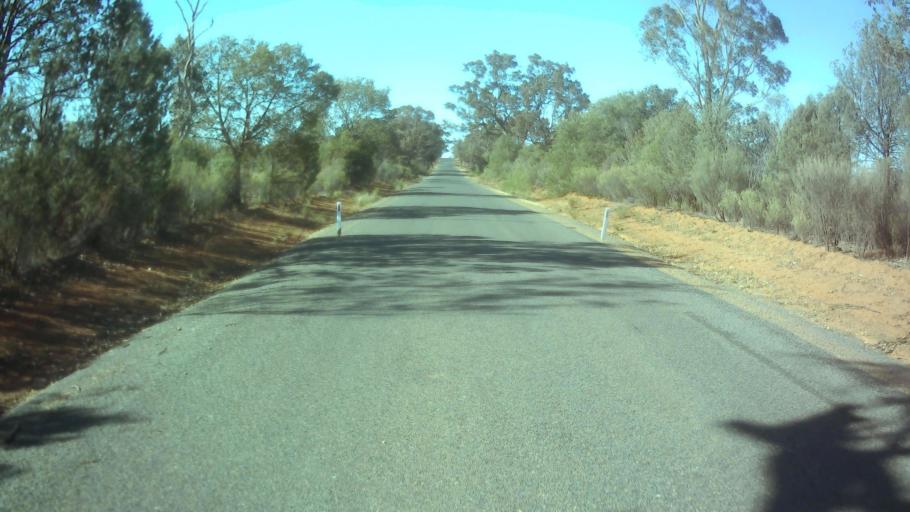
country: AU
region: New South Wales
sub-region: Forbes
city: Forbes
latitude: -33.7096
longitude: 147.8049
